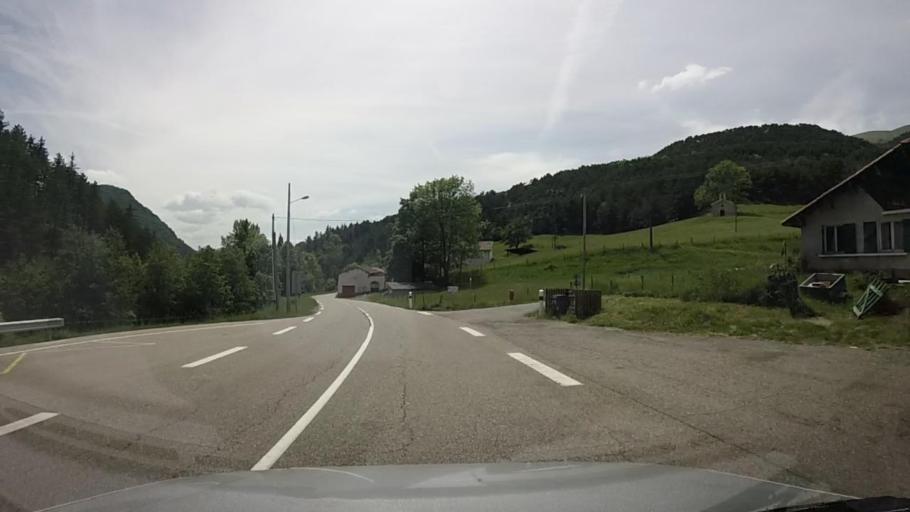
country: FR
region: Provence-Alpes-Cote d'Azur
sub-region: Departement des Alpes-de-Haute-Provence
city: Le Brusquet
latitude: 44.2371
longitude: 6.3586
